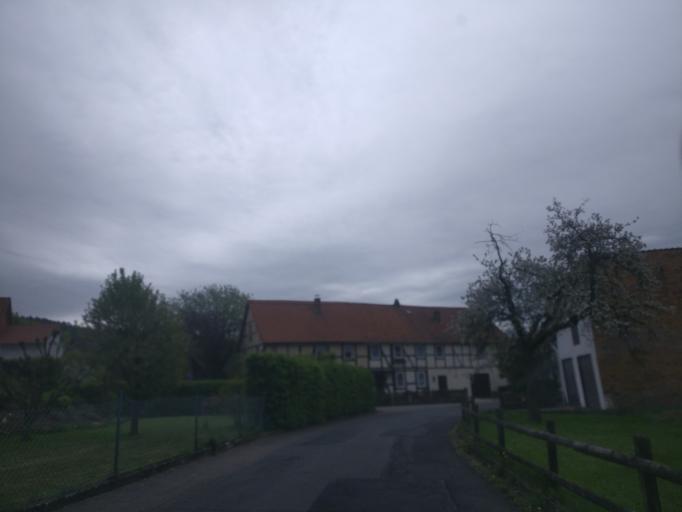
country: DE
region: Lower Saxony
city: Hannoversch Munden
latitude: 51.4459
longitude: 9.6624
